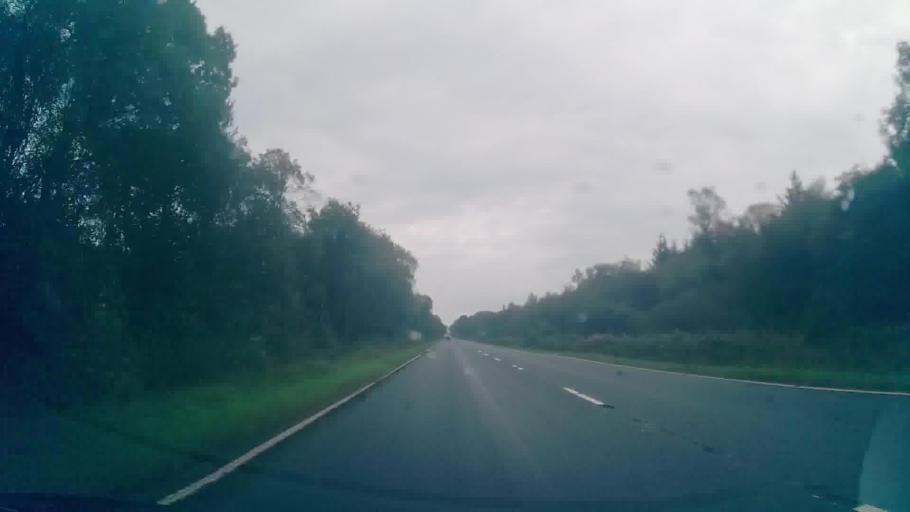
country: GB
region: Scotland
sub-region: Dumfries and Galloway
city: Annan
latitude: 55.0112
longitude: -3.3459
